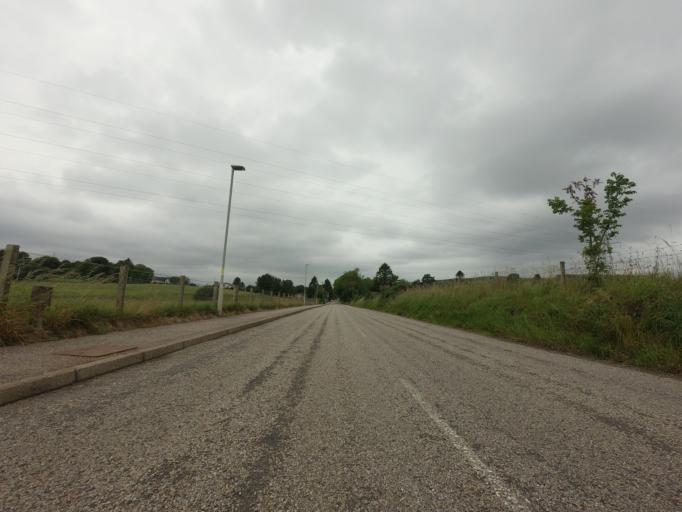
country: GB
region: Scotland
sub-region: Highland
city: Alness
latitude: 57.8854
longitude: -4.3705
